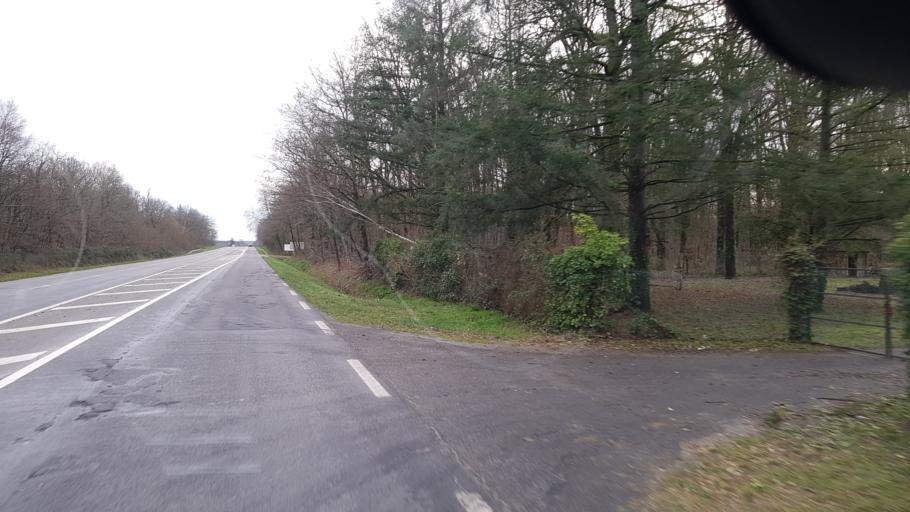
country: FR
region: Centre
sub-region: Departement du Loir-et-Cher
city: Nouan-le-Fuzelier
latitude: 47.5637
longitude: 2.0310
